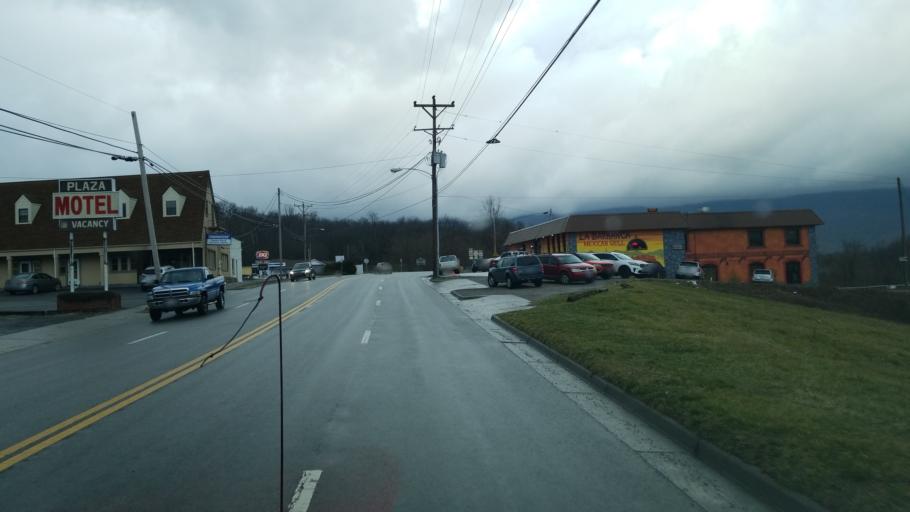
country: US
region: Virginia
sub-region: Giles County
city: Pearisburg
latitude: 37.3299
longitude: -80.7374
